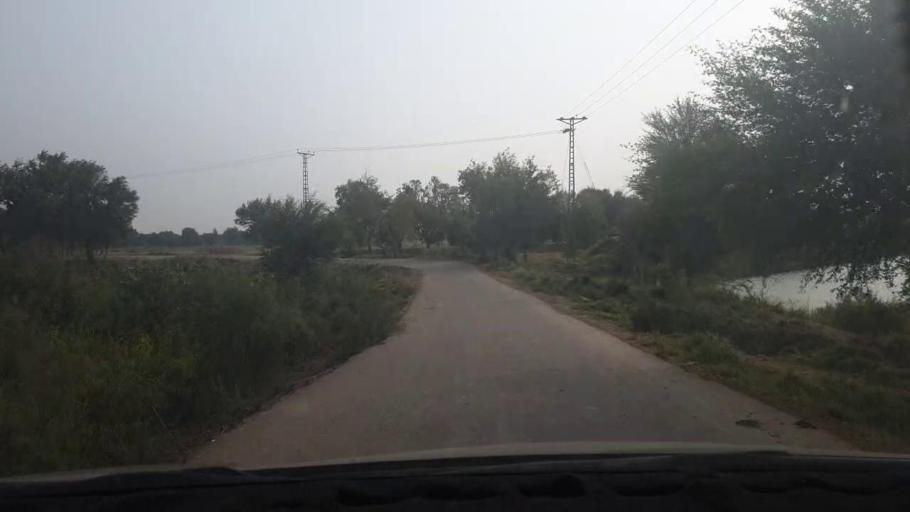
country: PK
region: Sindh
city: Jamshoro
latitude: 25.5073
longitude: 68.3144
